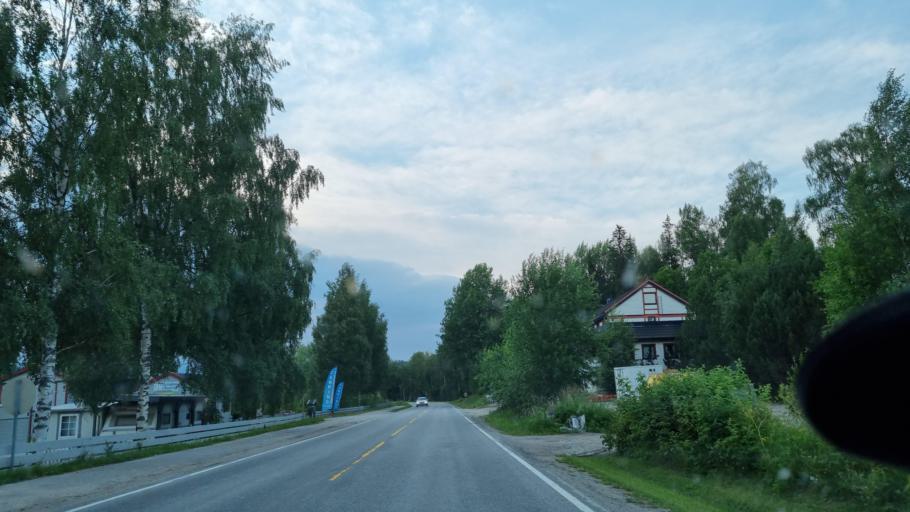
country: NO
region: Hedmark
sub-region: Trysil
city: Innbygda
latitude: 61.3036
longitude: 12.2752
